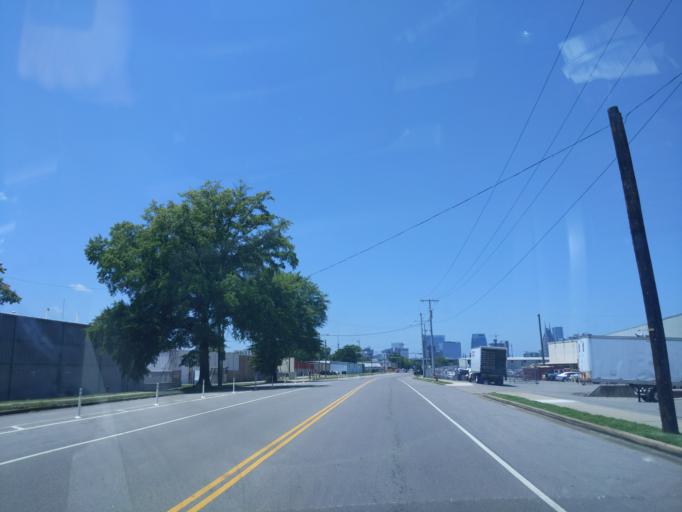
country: US
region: Tennessee
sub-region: Davidson County
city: Nashville
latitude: 36.1620
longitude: -86.7519
